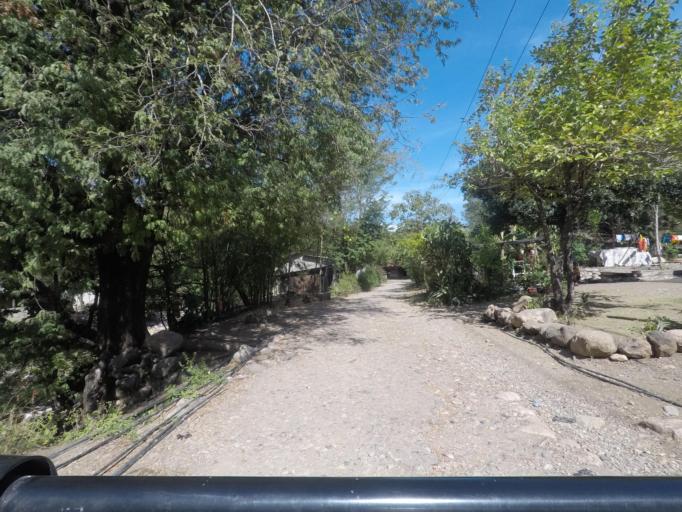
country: TL
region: Bobonaro
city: Maliana
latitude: -8.9922
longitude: 125.2182
